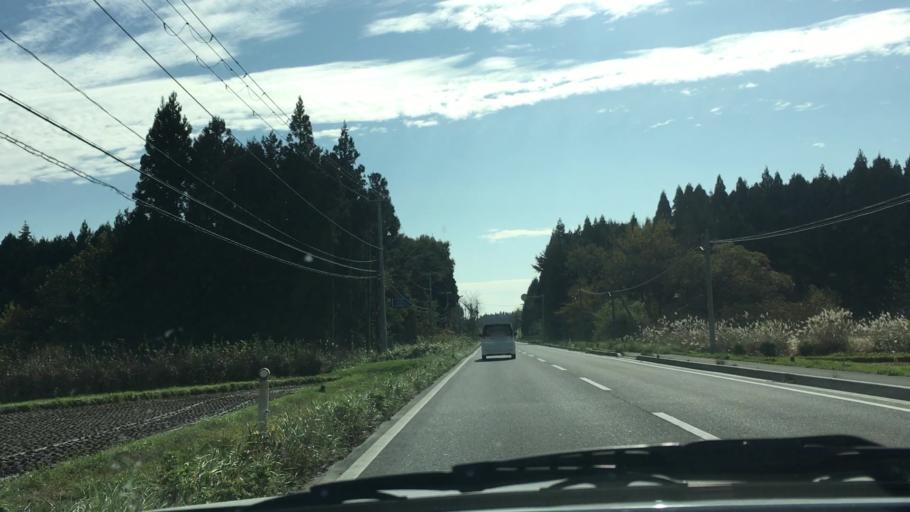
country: JP
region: Aomori
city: Hachinohe
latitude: 40.4333
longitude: 141.6884
